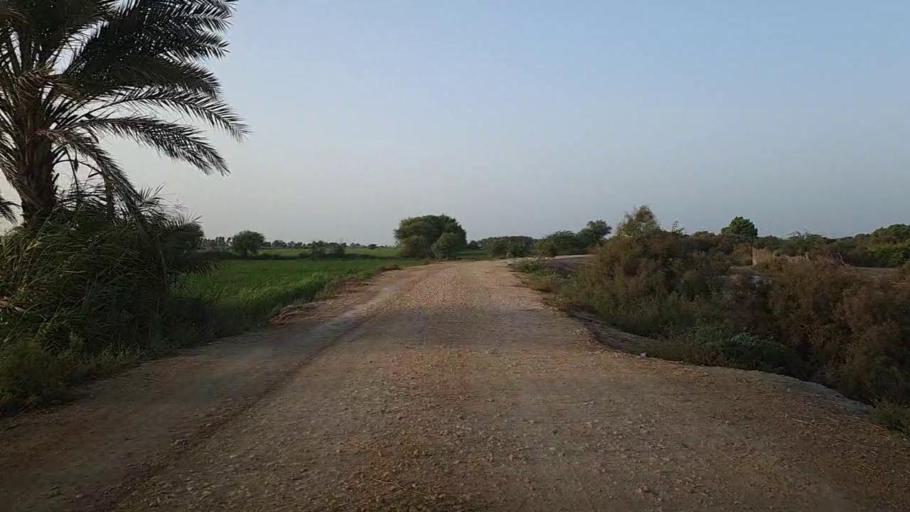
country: PK
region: Sindh
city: Kario
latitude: 24.7177
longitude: 68.4621
